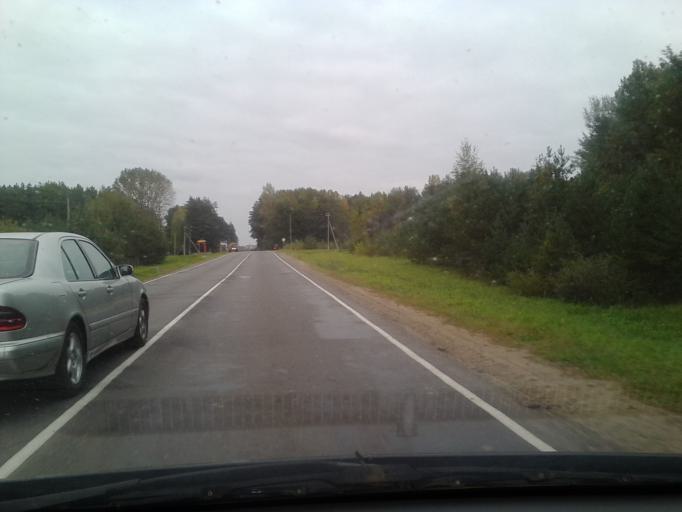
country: BY
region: Vitebsk
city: Pastavy
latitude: 55.0988
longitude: 26.8562
